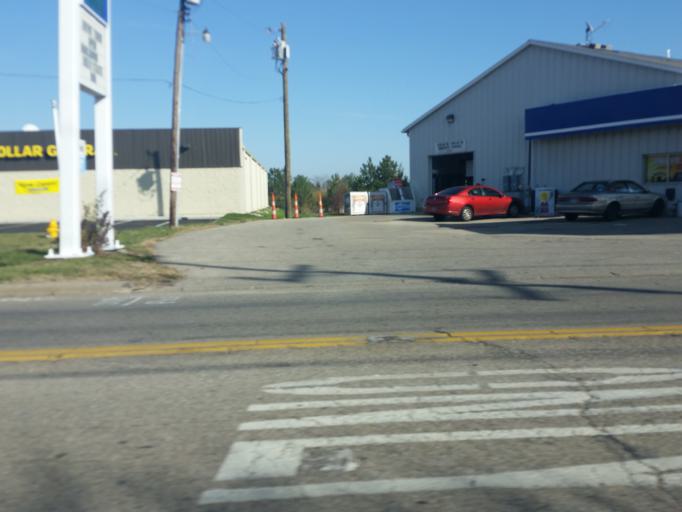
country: US
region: Ohio
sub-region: Butler County
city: Oxford
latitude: 39.4534
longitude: -84.6889
